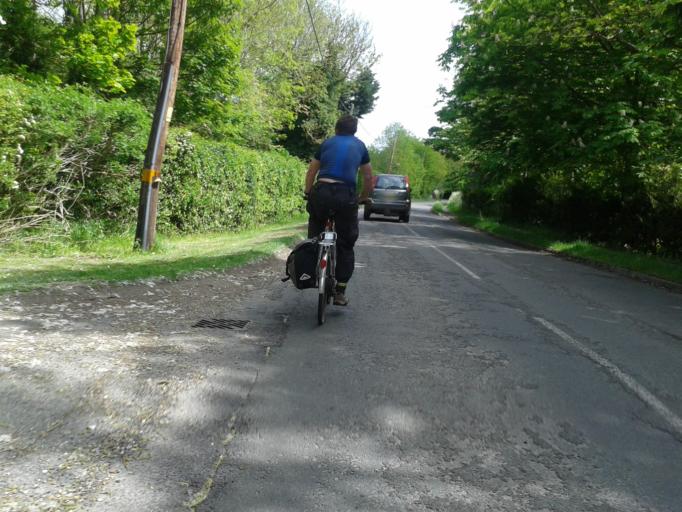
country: GB
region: England
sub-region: Cambridgeshire
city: Meldreth
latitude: 52.1242
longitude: 0.0219
